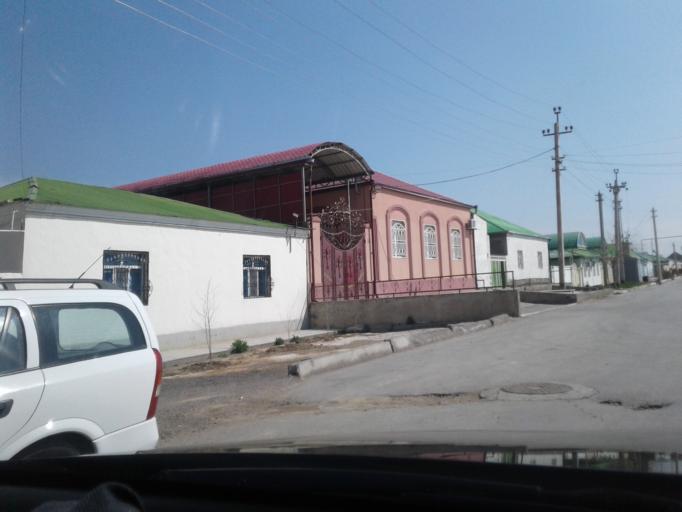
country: TM
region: Ahal
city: Ashgabat
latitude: 37.9866
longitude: 58.3971
